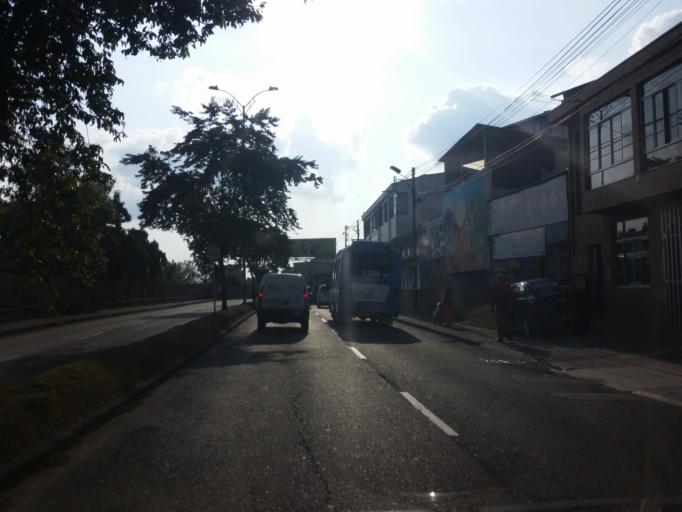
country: CO
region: Caldas
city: Manizales
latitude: 5.0609
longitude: -75.4942
